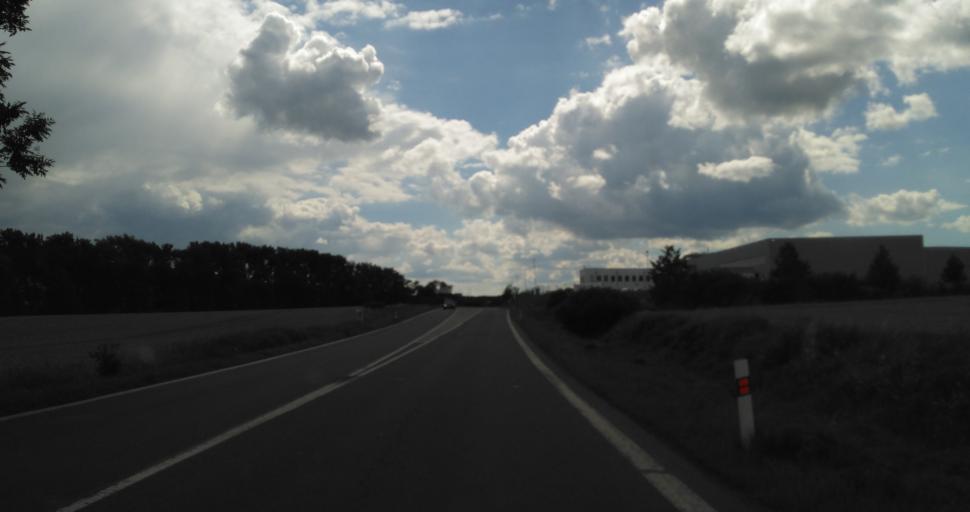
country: CZ
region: Central Bohemia
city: Komarov
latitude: 49.8451
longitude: 13.8247
